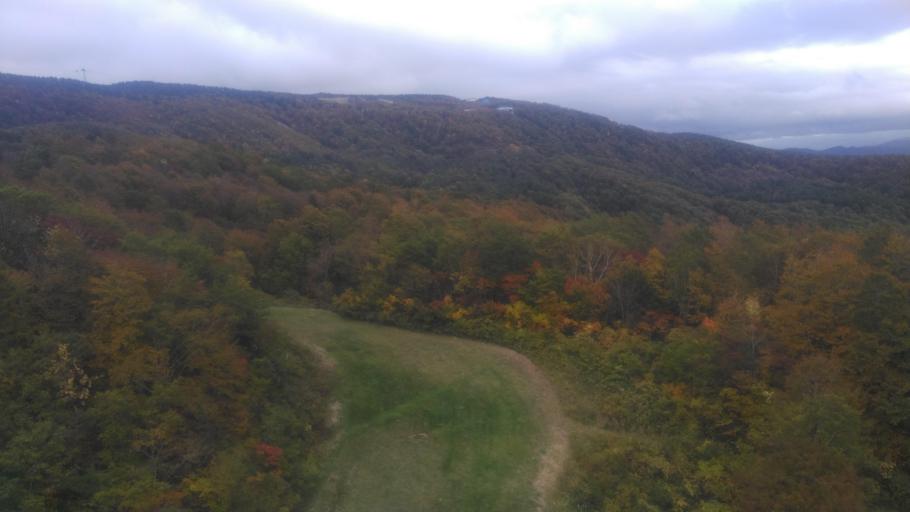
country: JP
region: Yamagata
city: Yamagata-shi
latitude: 38.1650
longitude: 140.4101
